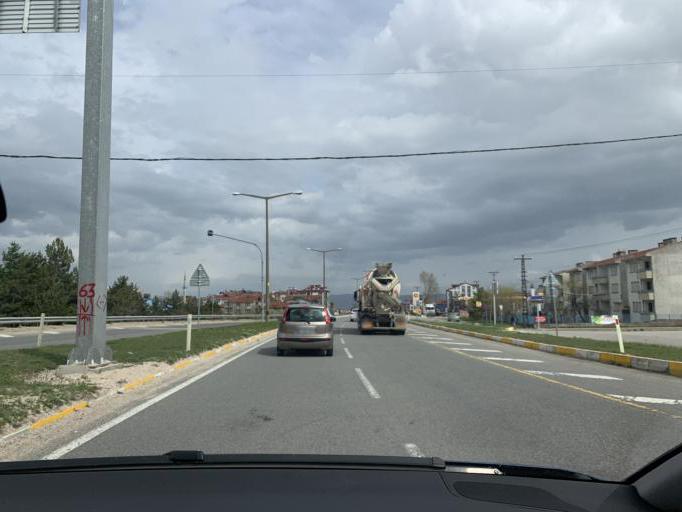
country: TR
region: Bolu
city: Gerede
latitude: 40.7985
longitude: 32.1869
